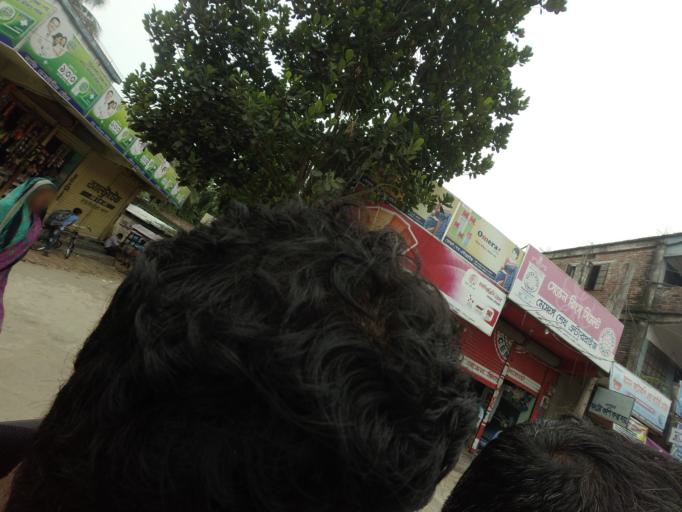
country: BD
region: Khulna
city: Kalia
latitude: 23.1804
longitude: 89.6478
